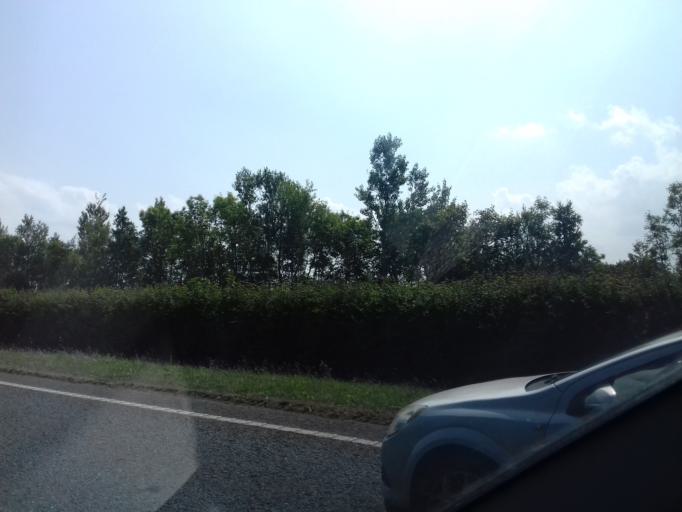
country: IE
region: Leinster
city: Balrothery
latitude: 53.5896
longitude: -6.2131
